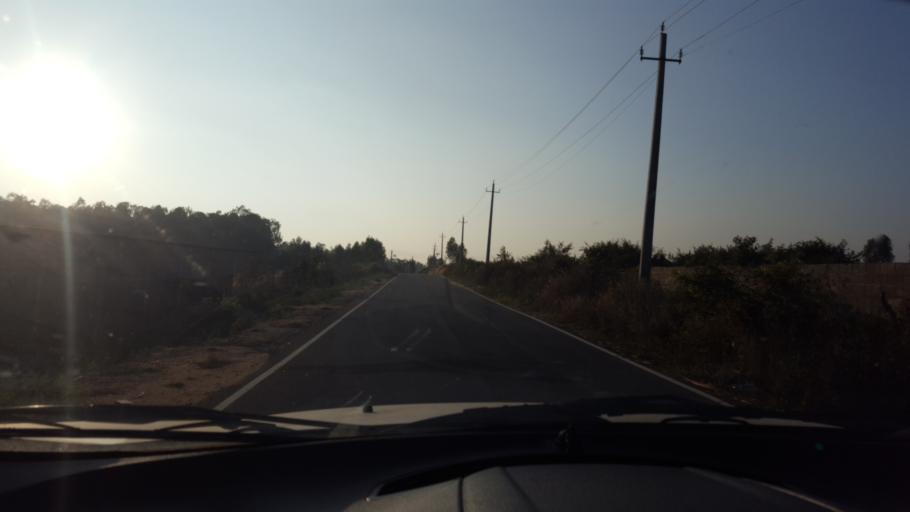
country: IN
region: Karnataka
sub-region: Bangalore Urban
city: Yelahanka
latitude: 13.1897
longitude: 77.6027
